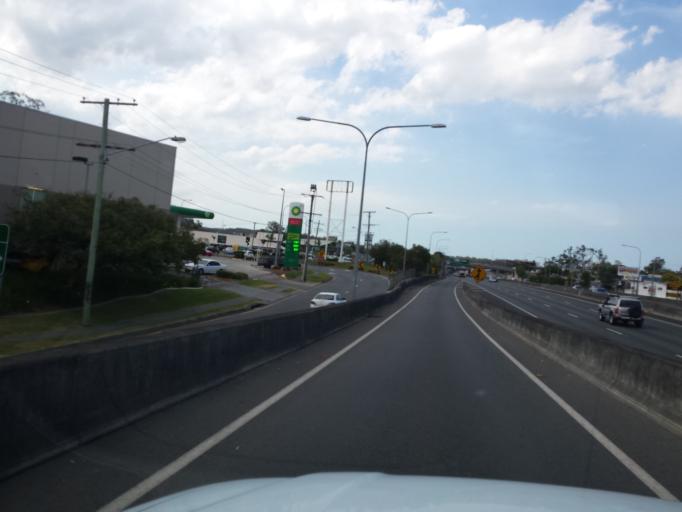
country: AU
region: Queensland
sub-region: Gold Coast
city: Nerang
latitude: -28.0001
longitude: 153.3395
